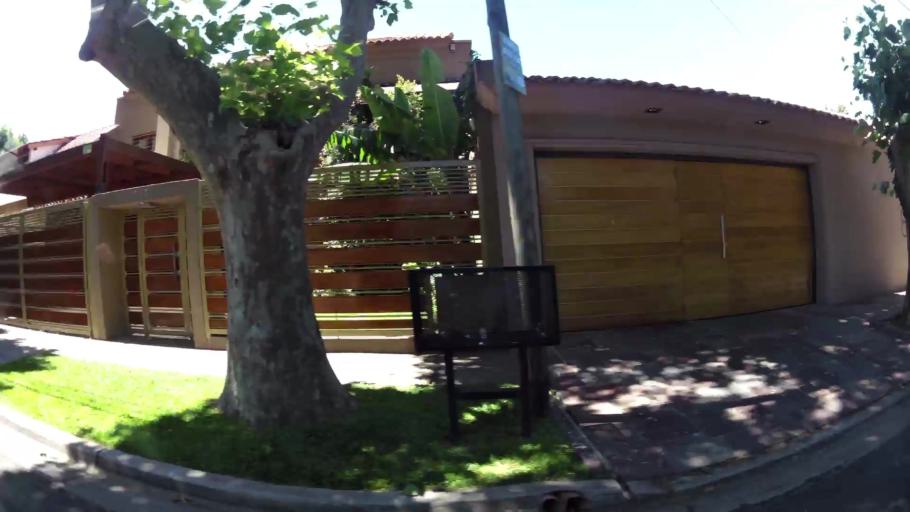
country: AR
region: Buenos Aires
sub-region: Partido de San Isidro
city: San Isidro
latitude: -34.5152
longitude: -58.5435
